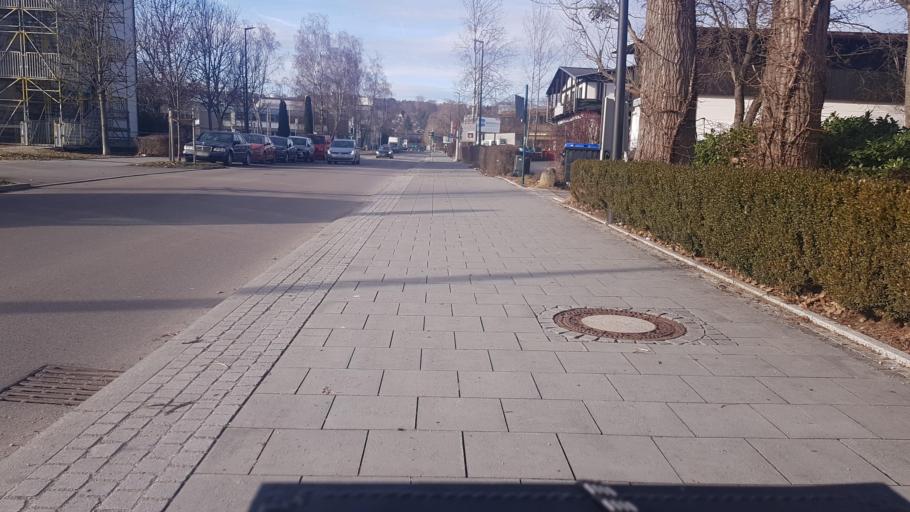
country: DE
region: Bavaria
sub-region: Upper Bavaria
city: Starnberg
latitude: 48.0036
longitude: 11.3533
